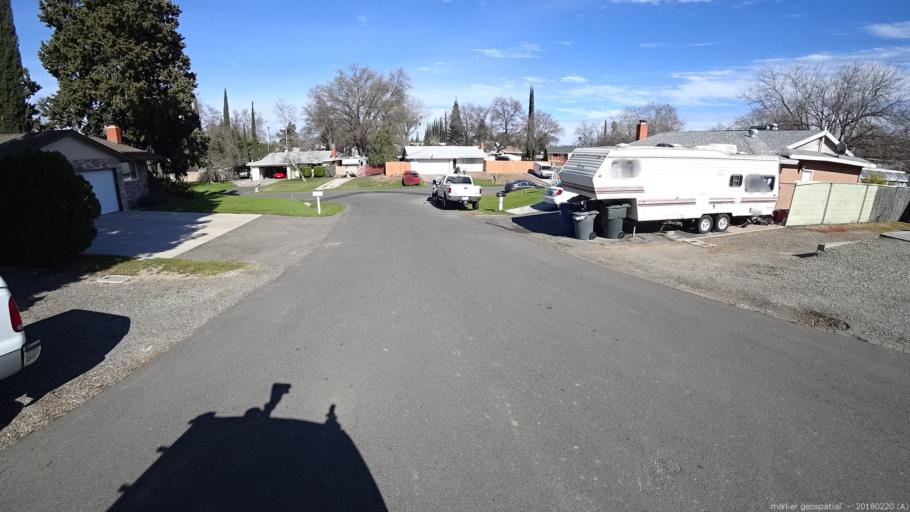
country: US
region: California
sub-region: Sacramento County
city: Orangevale
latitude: 38.6918
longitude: -121.2288
